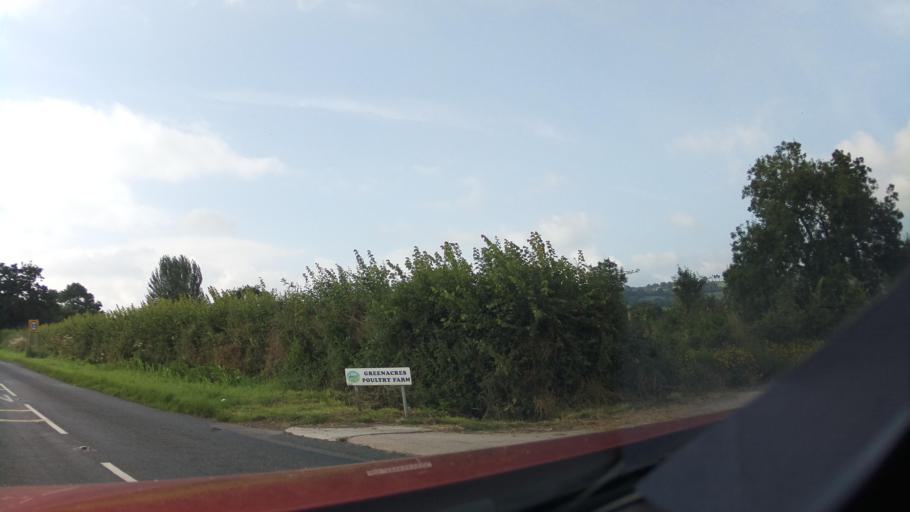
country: GB
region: England
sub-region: Bath and North East Somerset
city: Compton Martin
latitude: 51.3180
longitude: -2.6378
